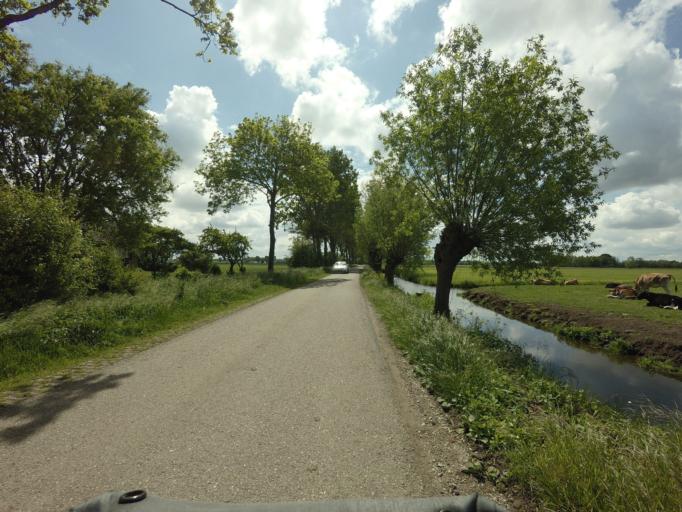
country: NL
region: South Holland
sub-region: Gemeente Gorinchem
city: Gorinchem
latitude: 51.8609
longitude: 4.9395
